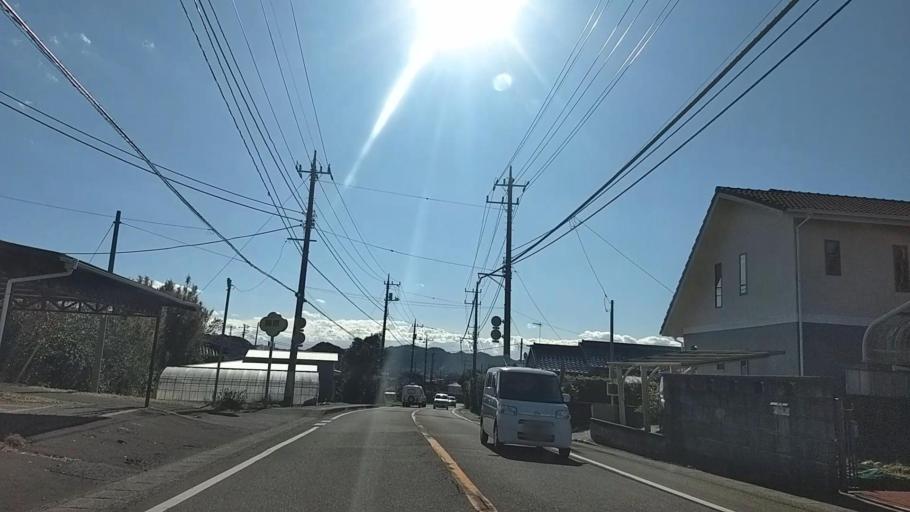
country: JP
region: Chiba
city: Tateyama
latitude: 34.9456
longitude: 139.8363
